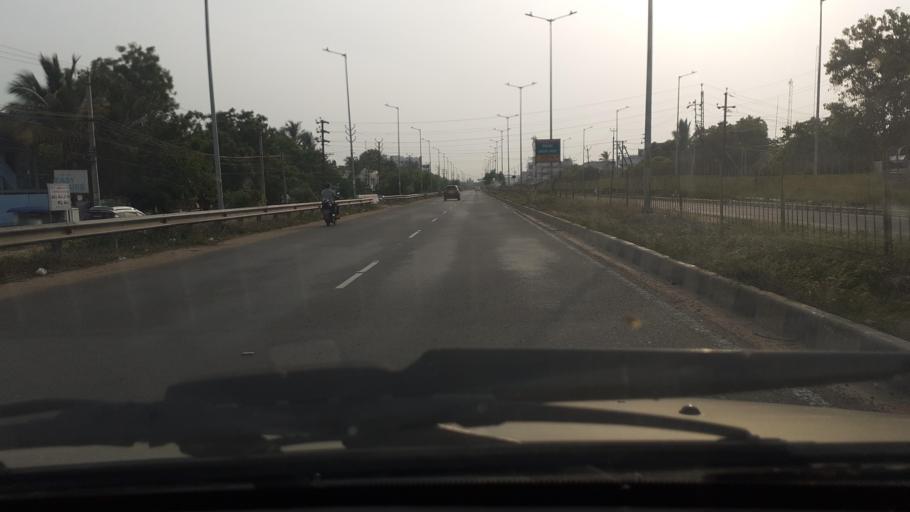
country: IN
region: Tamil Nadu
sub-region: Tirunelveli Kattabo
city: Tirunelveli
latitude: 8.7137
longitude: 77.7774
